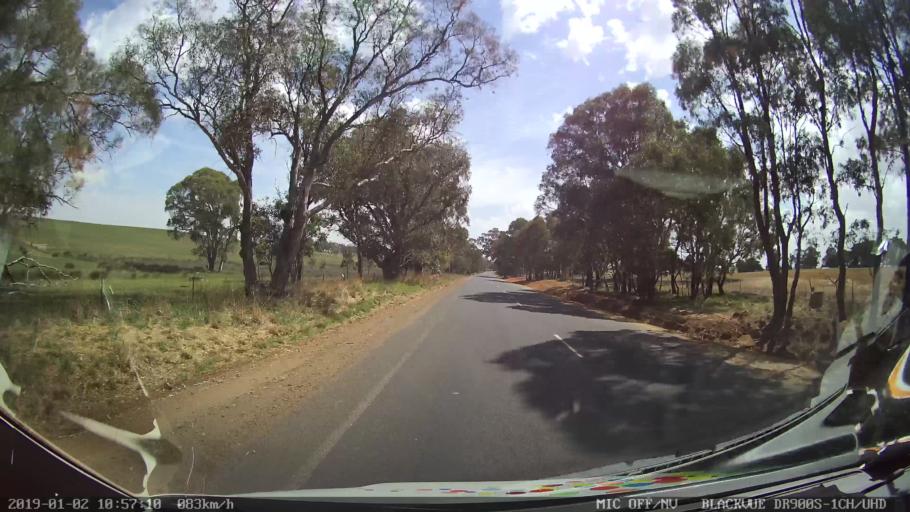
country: AU
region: New South Wales
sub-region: Cootamundra
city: Cootamundra
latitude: -34.6385
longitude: 148.2811
